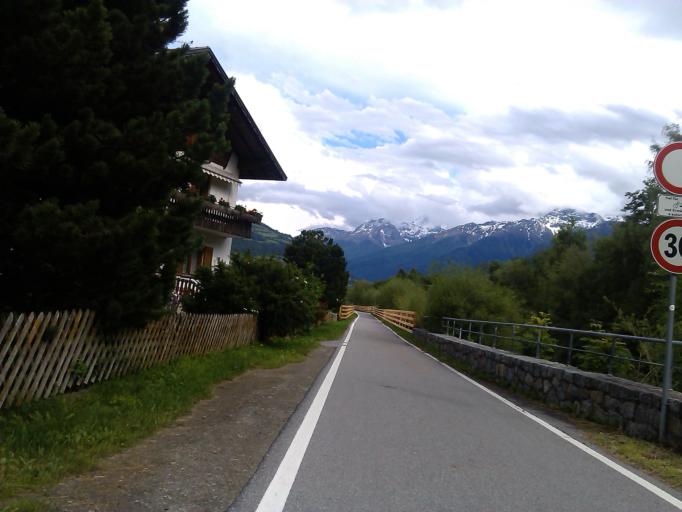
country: IT
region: Trentino-Alto Adige
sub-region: Bolzano
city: Glorenza
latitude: 46.6687
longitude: 10.5555
